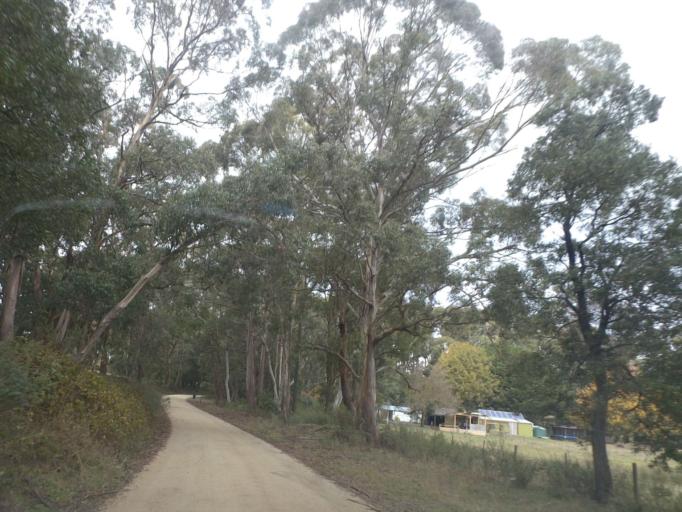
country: AU
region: Victoria
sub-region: Moorabool
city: Bacchus Marsh
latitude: -37.3992
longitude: 144.3464
